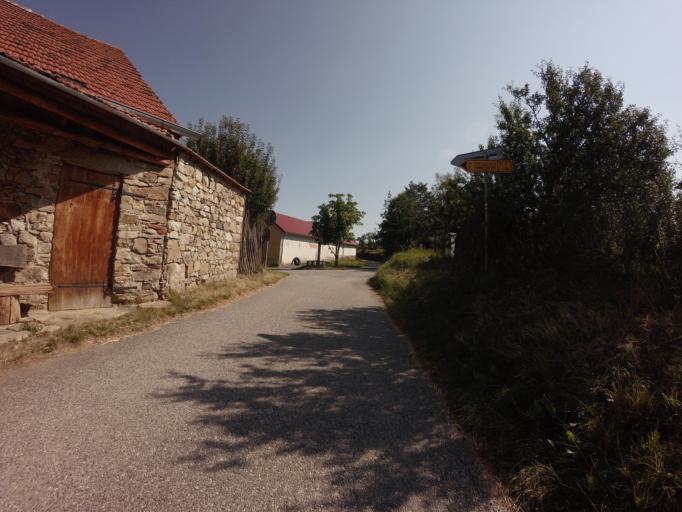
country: CZ
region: Jihocesky
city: Kamenny Ujezd
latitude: 48.8646
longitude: 14.3792
